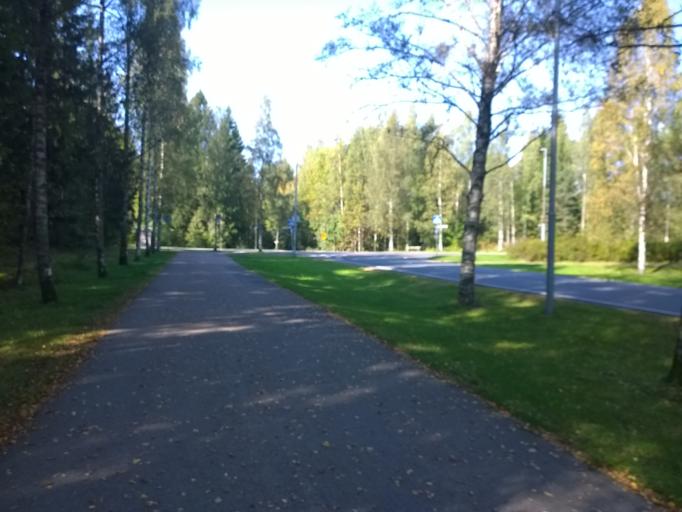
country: FI
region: Pirkanmaa
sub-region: Tampere
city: Tampere
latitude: 61.4495
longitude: 23.8320
